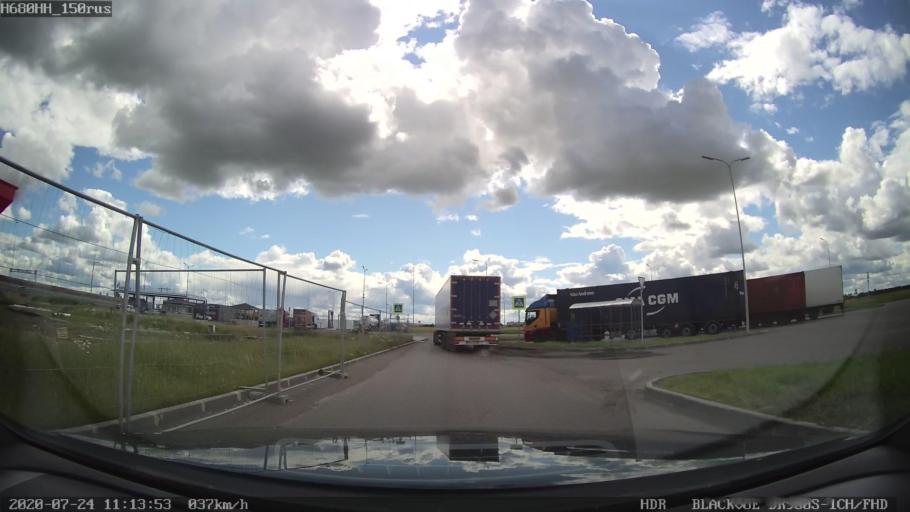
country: RU
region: Leningrad
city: Fedorovskoye
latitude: 59.7011
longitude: 30.5512
